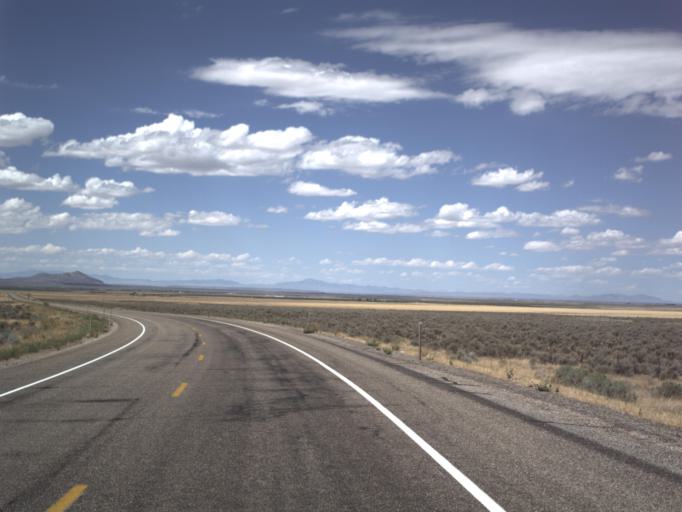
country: US
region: Utah
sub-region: Millard County
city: Fillmore
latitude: 39.1133
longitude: -112.2765
